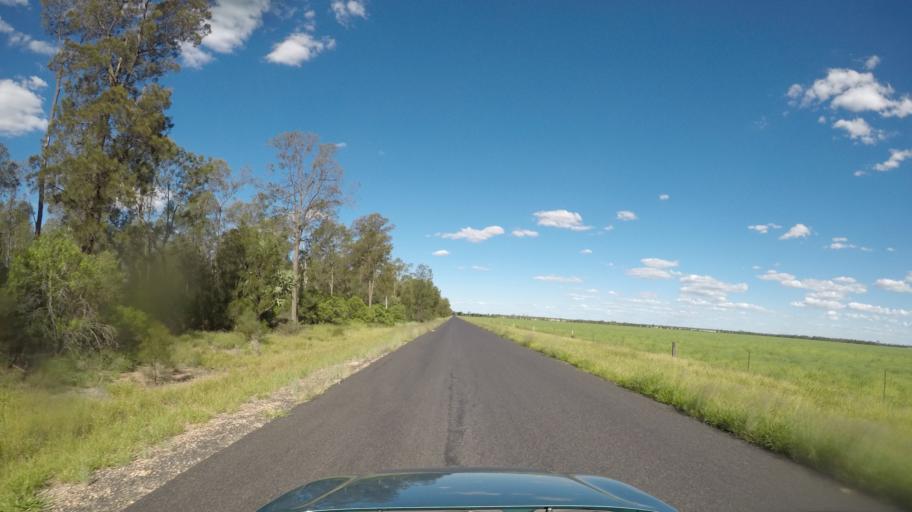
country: AU
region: Queensland
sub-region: Goondiwindi
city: Goondiwindi
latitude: -28.1544
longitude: 150.3628
